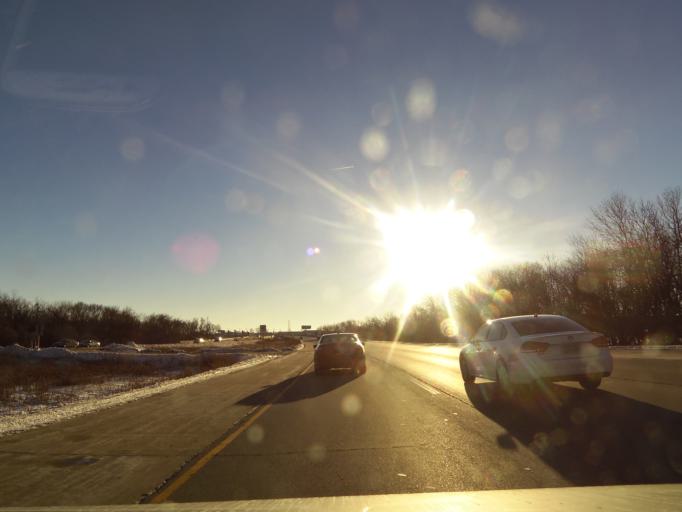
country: US
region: Wisconsin
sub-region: Racine County
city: Caledonia
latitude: 42.8467
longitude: -87.9489
